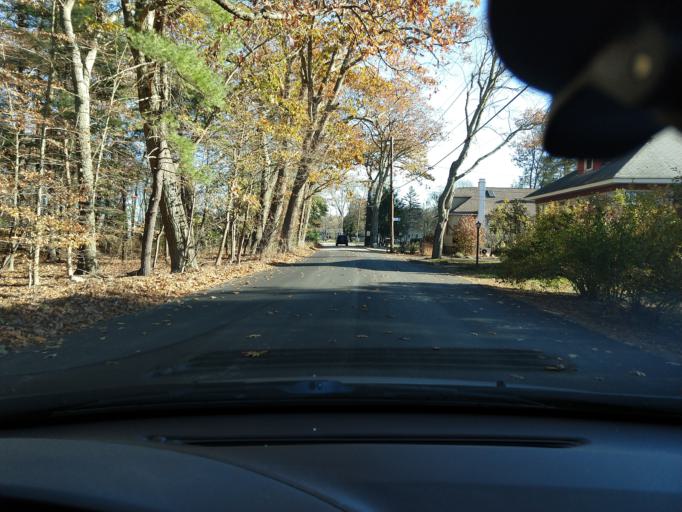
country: US
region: Massachusetts
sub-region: Middlesex County
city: Bedford
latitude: 42.4726
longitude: -71.2758
